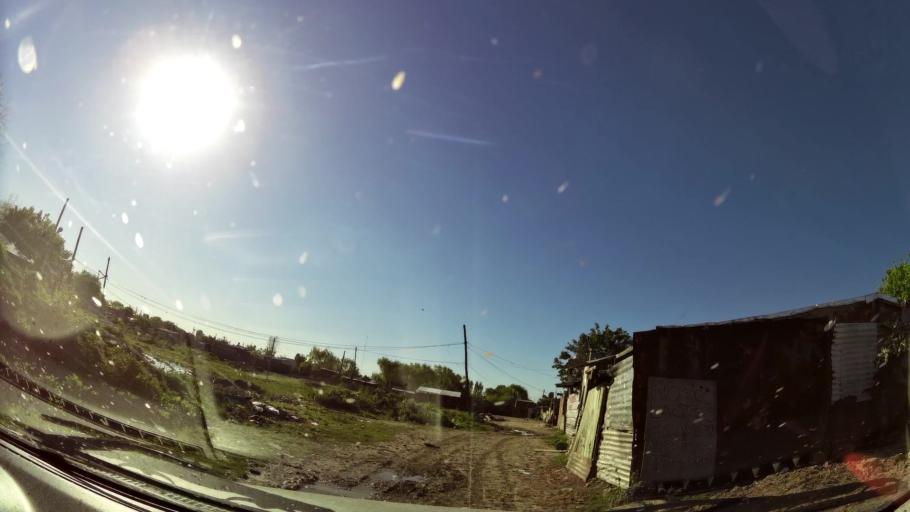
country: AR
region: Buenos Aires
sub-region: Partido de Quilmes
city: Quilmes
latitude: -34.7528
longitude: -58.3184
